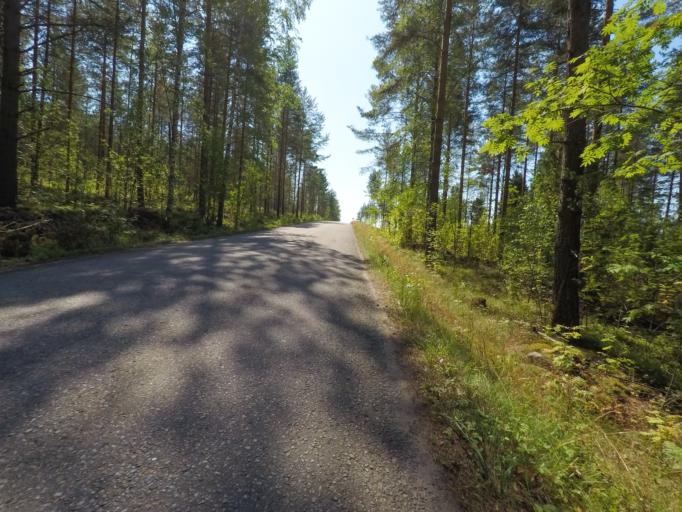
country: FI
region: Southern Savonia
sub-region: Mikkeli
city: Puumala
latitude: 61.4183
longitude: 28.0929
